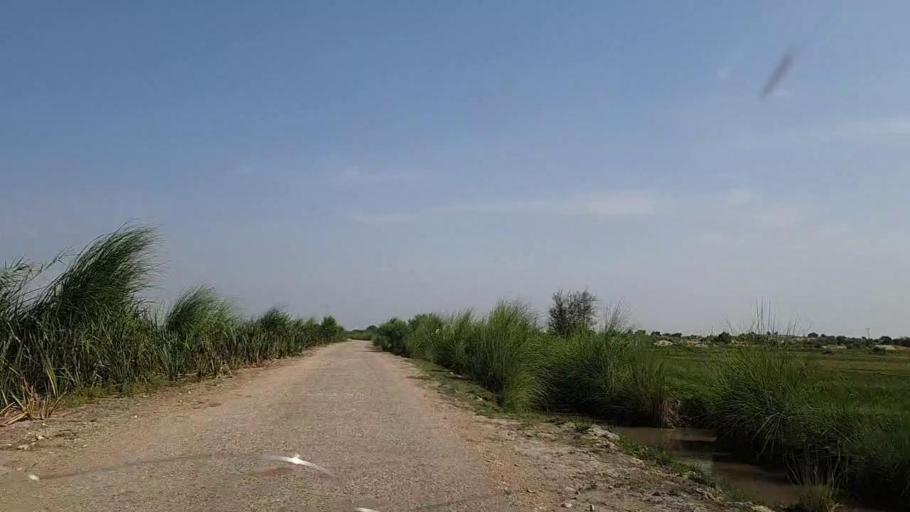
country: PK
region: Sindh
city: Khanpur
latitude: 27.7178
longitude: 69.3611
